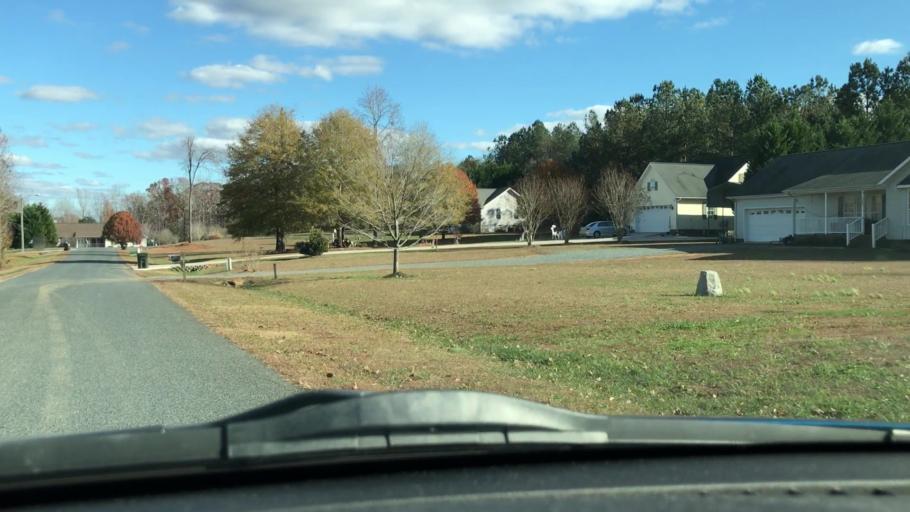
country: US
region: North Carolina
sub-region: Randolph County
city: Franklinville
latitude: 35.7140
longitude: -79.7332
